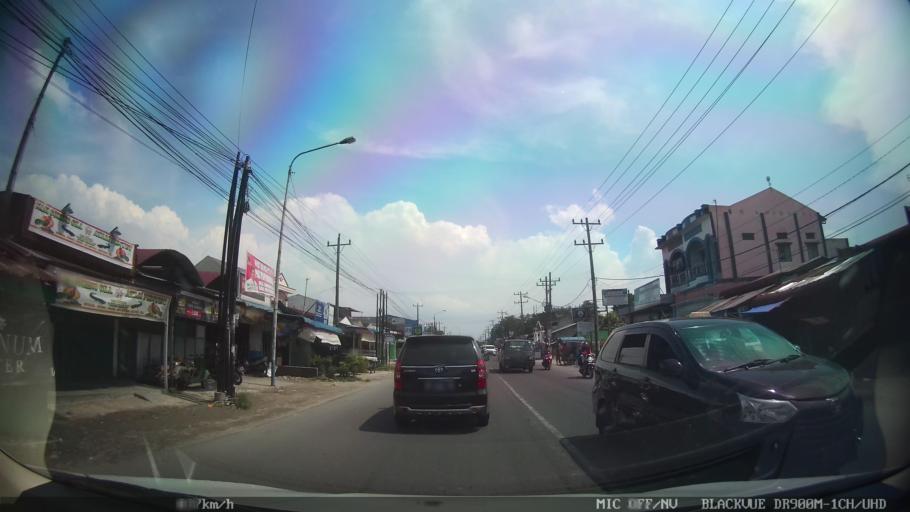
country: ID
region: North Sumatra
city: Medan
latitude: 3.6560
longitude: 98.6568
